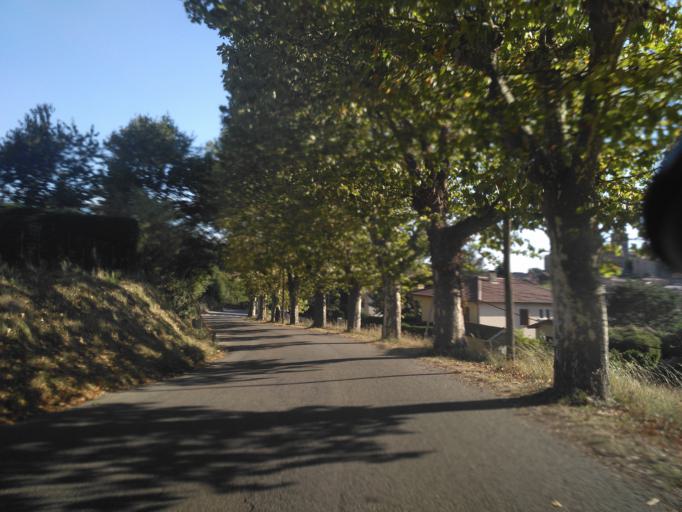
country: FR
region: Rhone-Alpes
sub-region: Departement de la Drome
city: Clerieux
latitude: 45.1253
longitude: 4.9857
